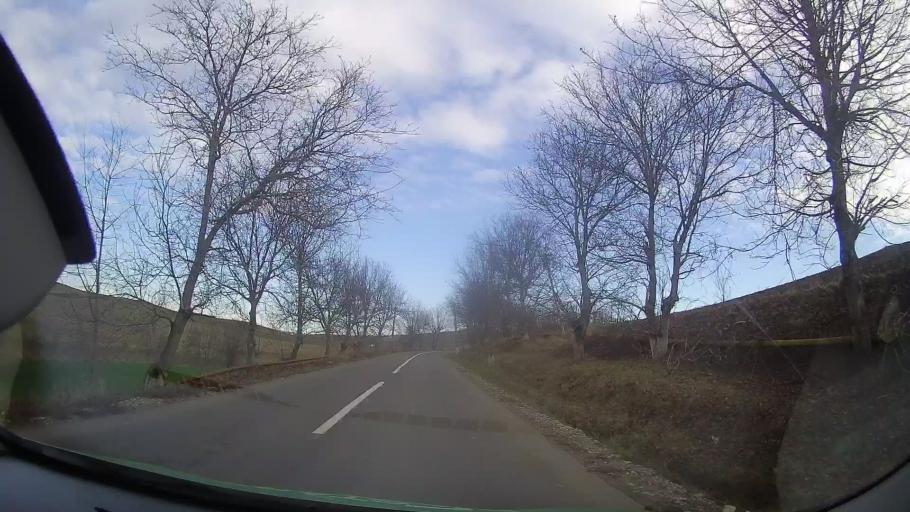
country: RO
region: Mures
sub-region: Comuna Iclanzel
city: Iclanzel
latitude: 46.5066
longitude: 24.2589
